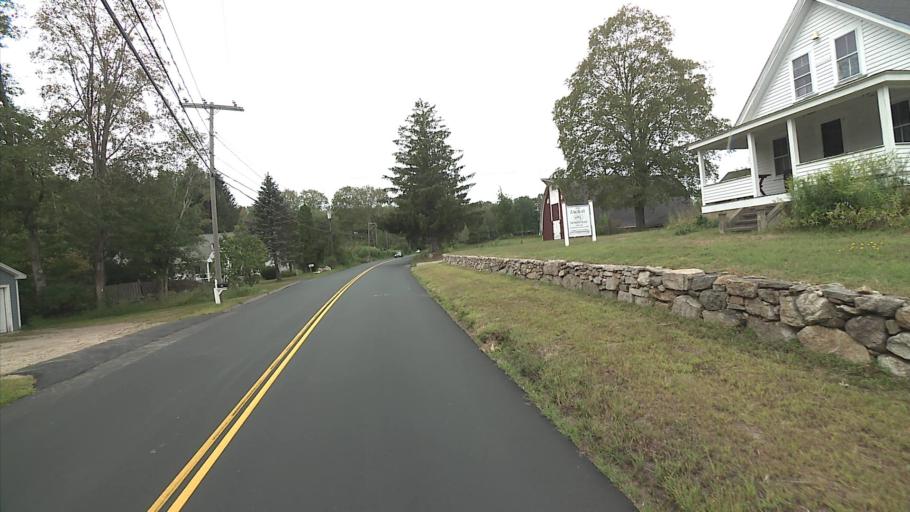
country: US
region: Connecticut
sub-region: New London County
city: Colchester
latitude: 41.5971
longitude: -72.3418
